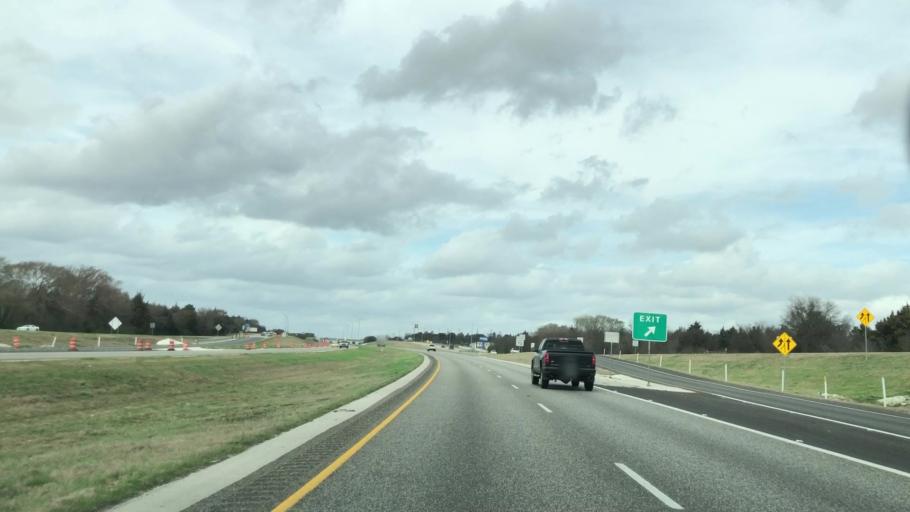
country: US
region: Texas
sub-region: Brazos County
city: Bryan
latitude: 30.6891
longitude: -96.3505
